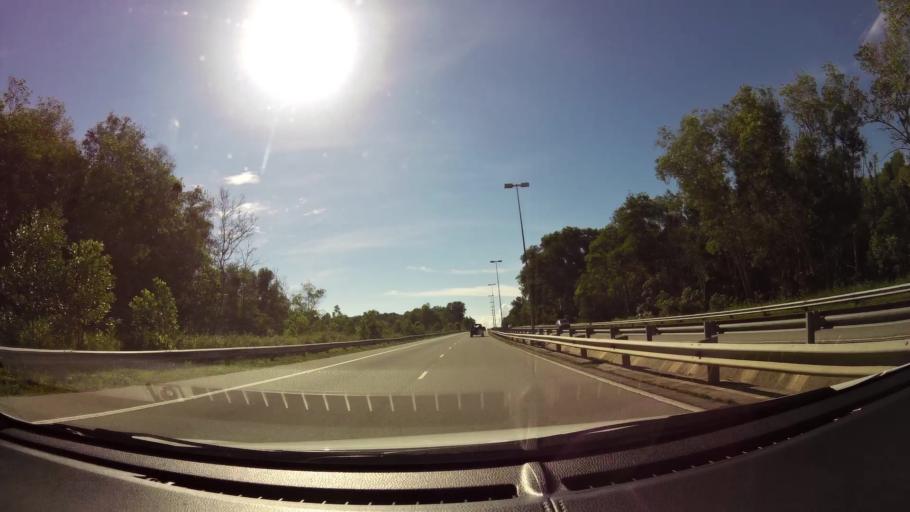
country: BN
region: Brunei and Muara
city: Bandar Seri Begawan
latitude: 4.9837
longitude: 114.9294
